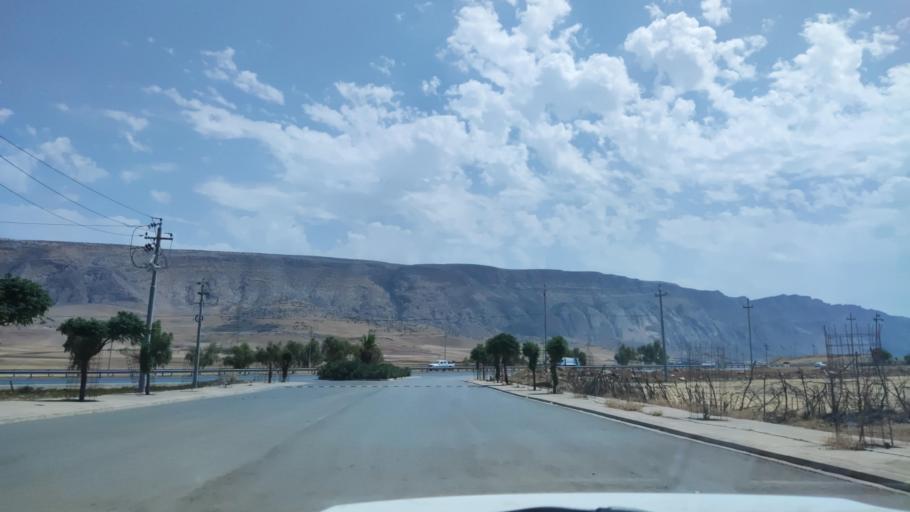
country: IQ
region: Arbil
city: Shaqlawah
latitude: 36.4968
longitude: 44.3626
